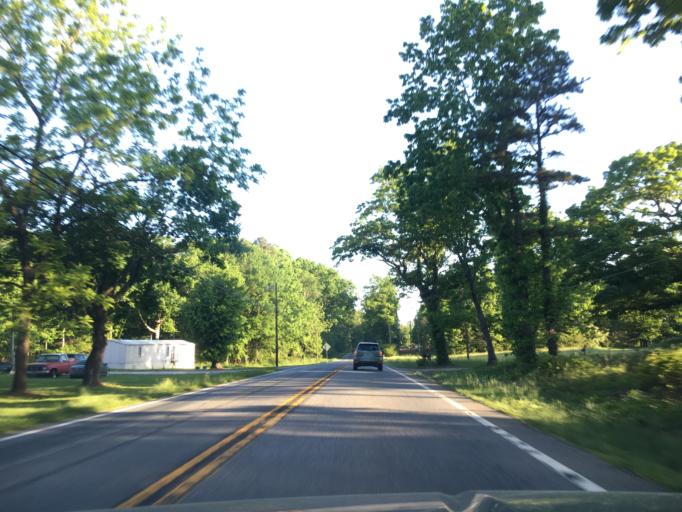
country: US
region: Virginia
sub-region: Campbell County
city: Rustburg
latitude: 37.2552
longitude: -79.1209
